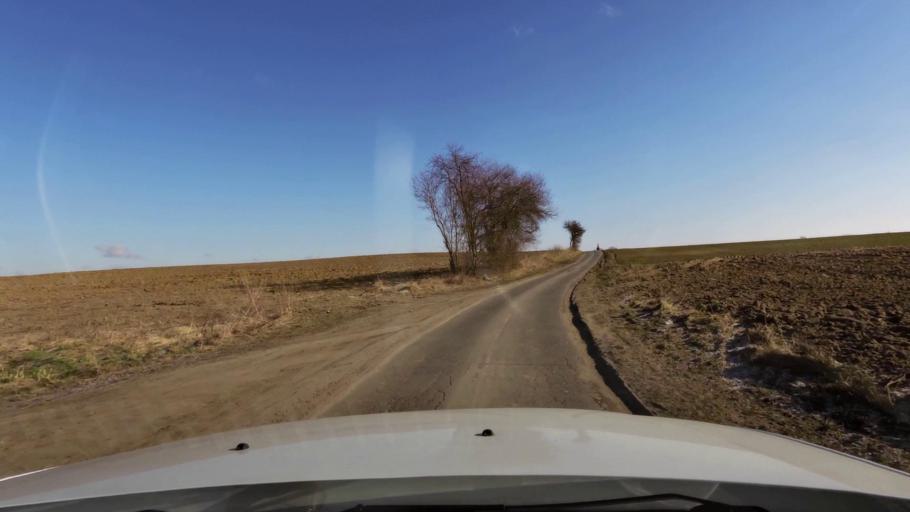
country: PL
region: West Pomeranian Voivodeship
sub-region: Powiat pyrzycki
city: Lipiany
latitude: 52.9880
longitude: 15.0434
